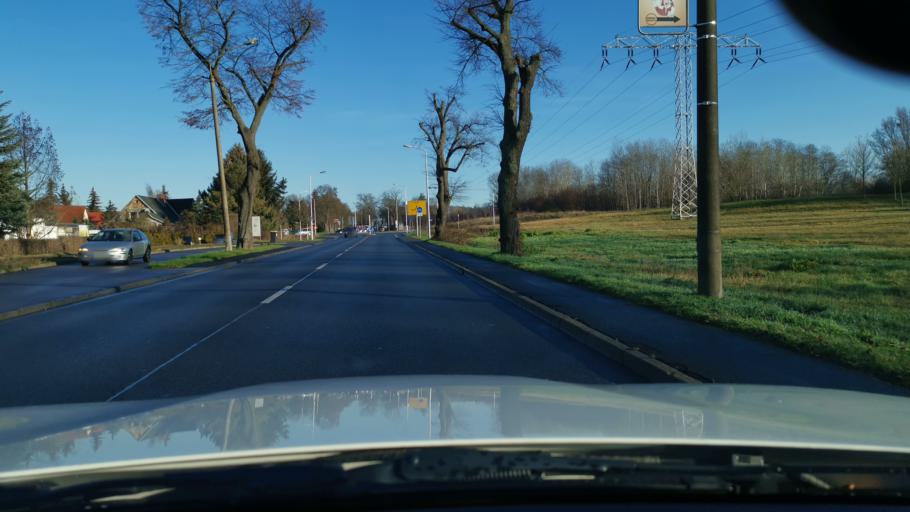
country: DE
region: Saxony-Anhalt
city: Wittenburg
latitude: 51.8854
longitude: 12.6591
